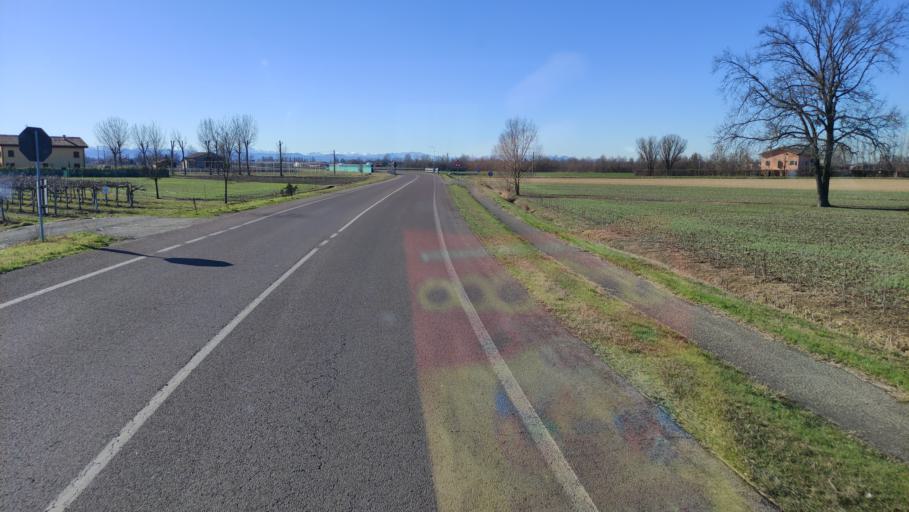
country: IT
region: Emilia-Romagna
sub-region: Provincia di Reggio Emilia
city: San Martino in Rio
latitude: 44.7487
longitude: 10.7839
